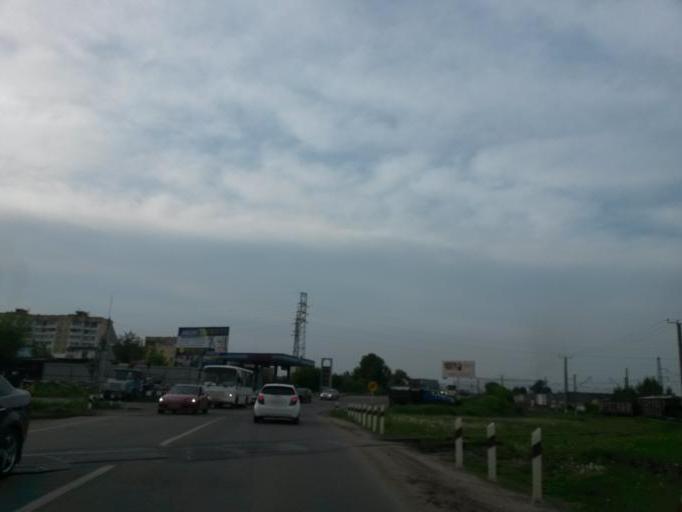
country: RU
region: Moskovskaya
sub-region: Chekhovskiy Rayon
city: Chekhov
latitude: 55.1418
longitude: 37.4896
